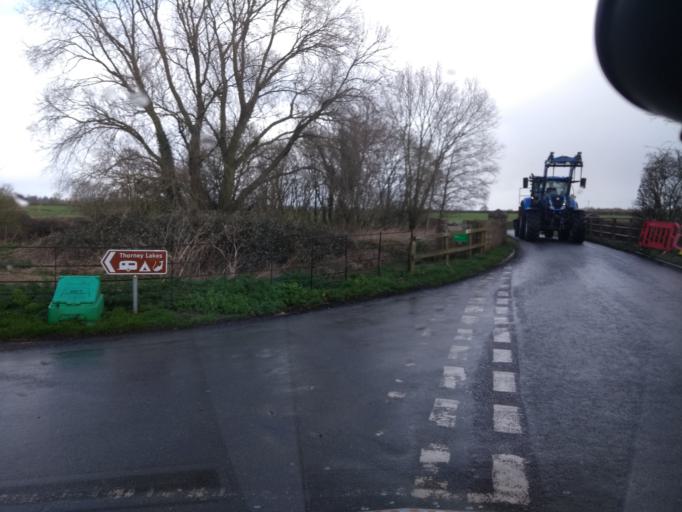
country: GB
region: England
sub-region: Somerset
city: Martock
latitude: 50.9759
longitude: -2.7938
